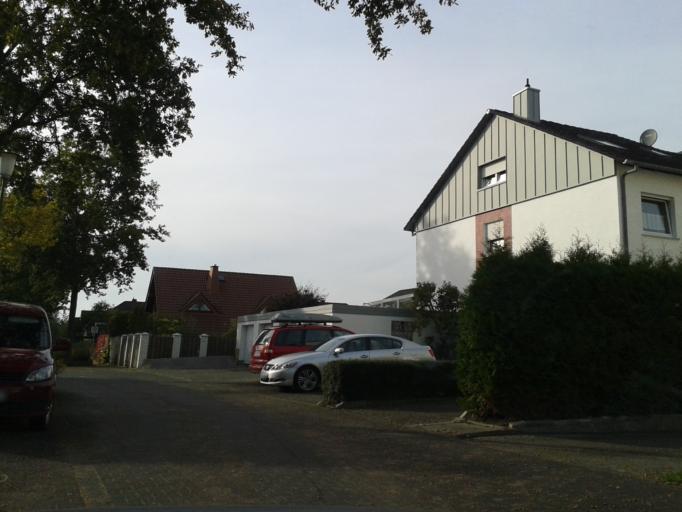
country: DE
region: North Rhine-Westphalia
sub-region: Regierungsbezirk Detmold
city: Paderborn
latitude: 51.7276
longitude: 8.6861
